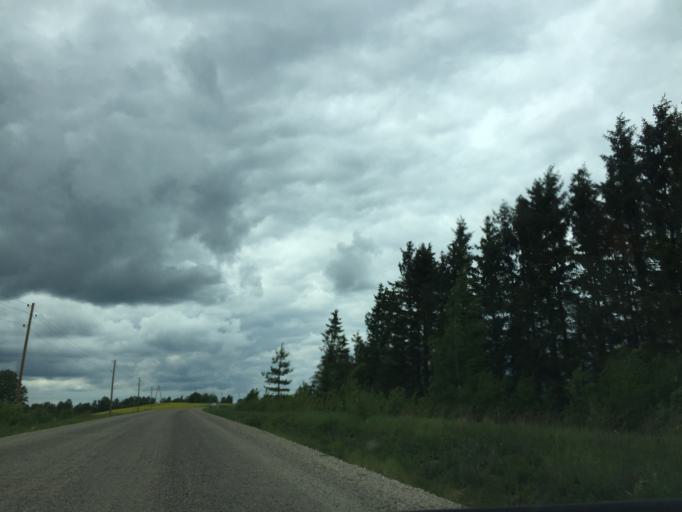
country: LV
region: Dagda
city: Dagda
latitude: 56.0469
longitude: 27.5772
